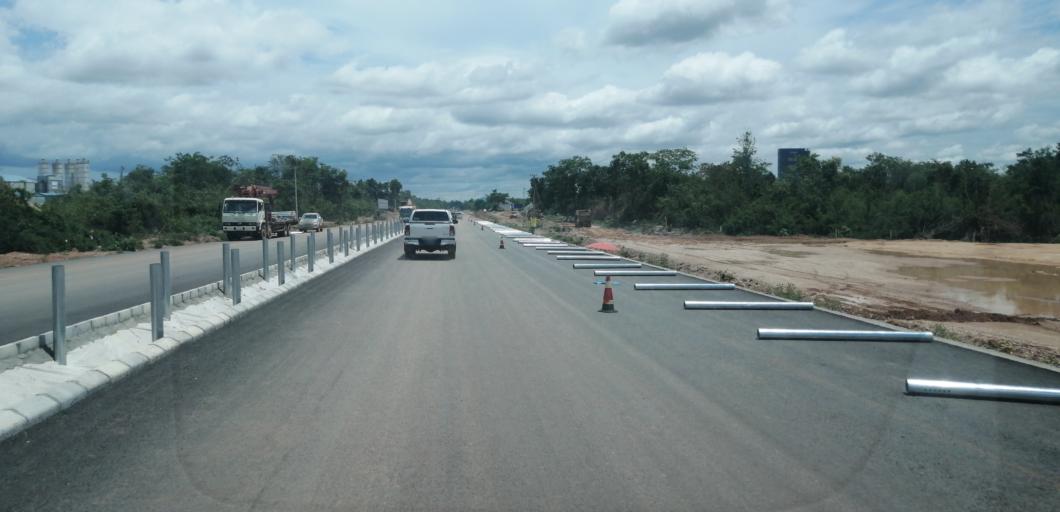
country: LA
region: Vientiane
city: Muang Phon-Hong
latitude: 18.2946
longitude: 102.4574
